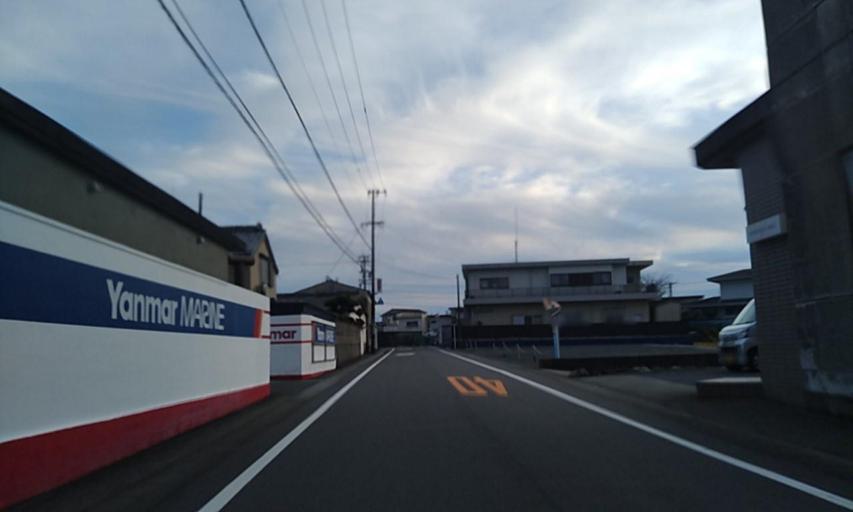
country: JP
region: Mie
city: Toba
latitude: 34.2834
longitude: 136.8856
